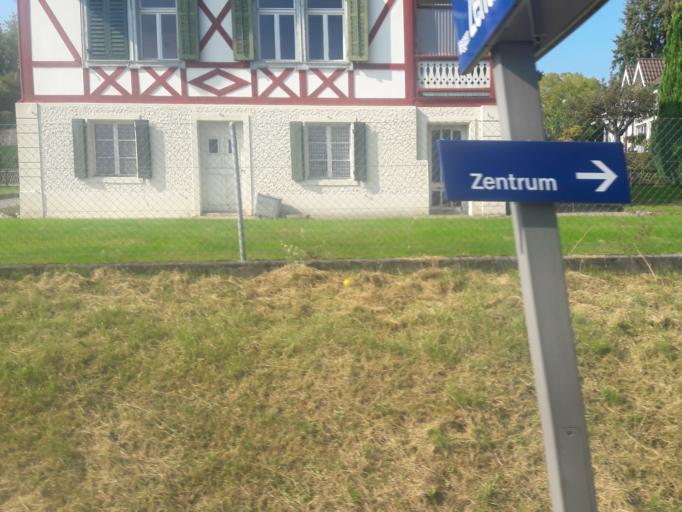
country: CH
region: Lucerne
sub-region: Lucerne-Land District
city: Meggen
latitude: 47.0449
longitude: 8.3739
